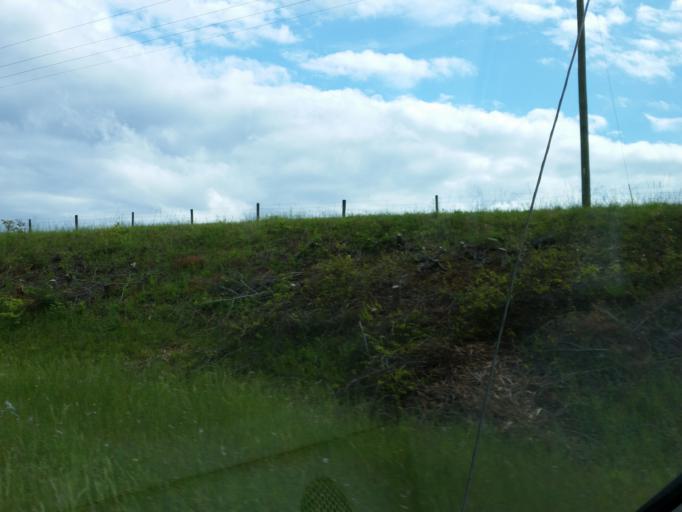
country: US
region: Georgia
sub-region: Crawford County
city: Roberta
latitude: 32.8077
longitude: -84.0499
